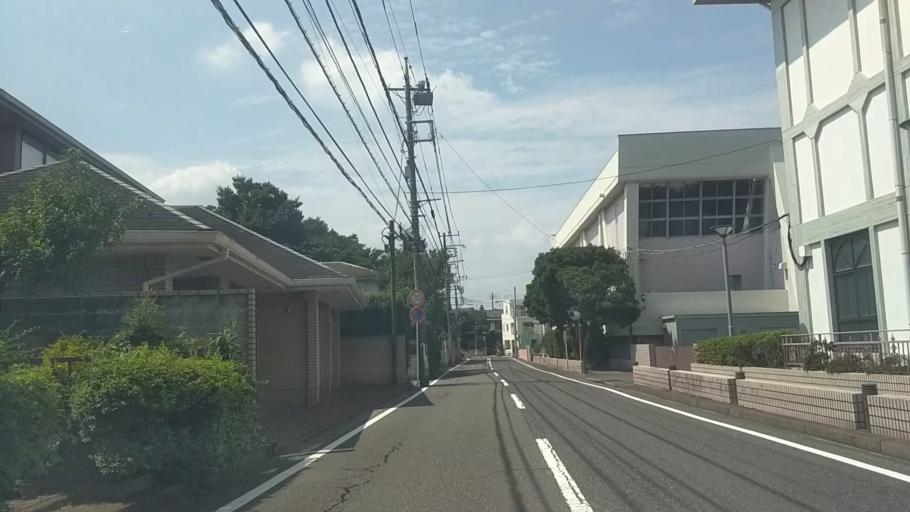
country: JP
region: Kanagawa
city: Yokohama
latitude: 35.4811
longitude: 139.6199
